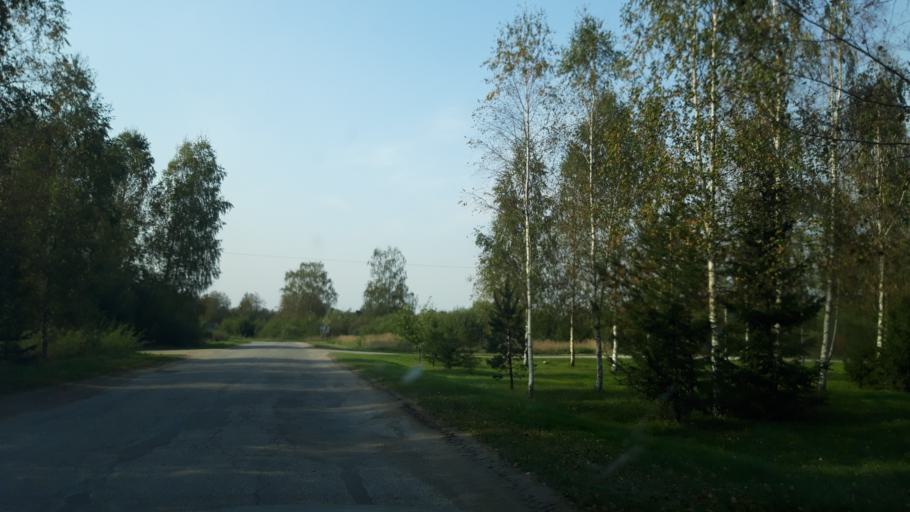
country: LV
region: Mazsalaca
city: Mazsalaca
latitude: 57.8526
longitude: 25.0383
